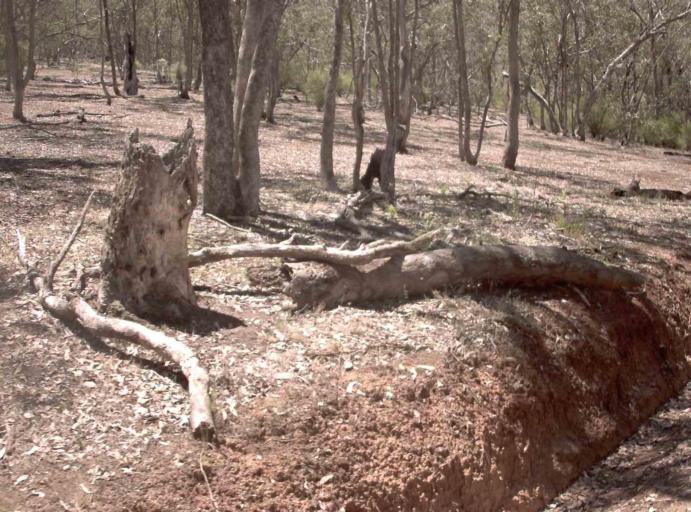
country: AU
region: New South Wales
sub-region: Snowy River
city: Jindabyne
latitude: -37.0891
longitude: 148.4128
